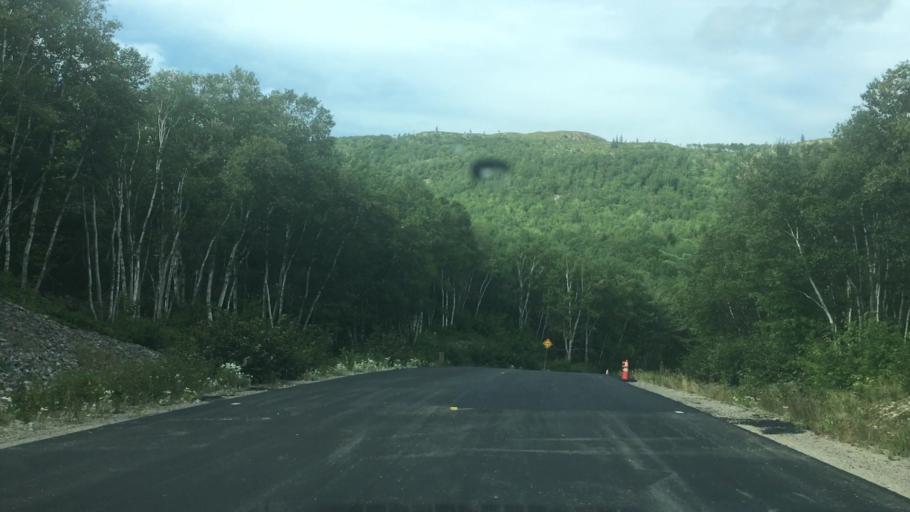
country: CA
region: Nova Scotia
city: Sydney Mines
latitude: 46.5712
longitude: -60.3940
